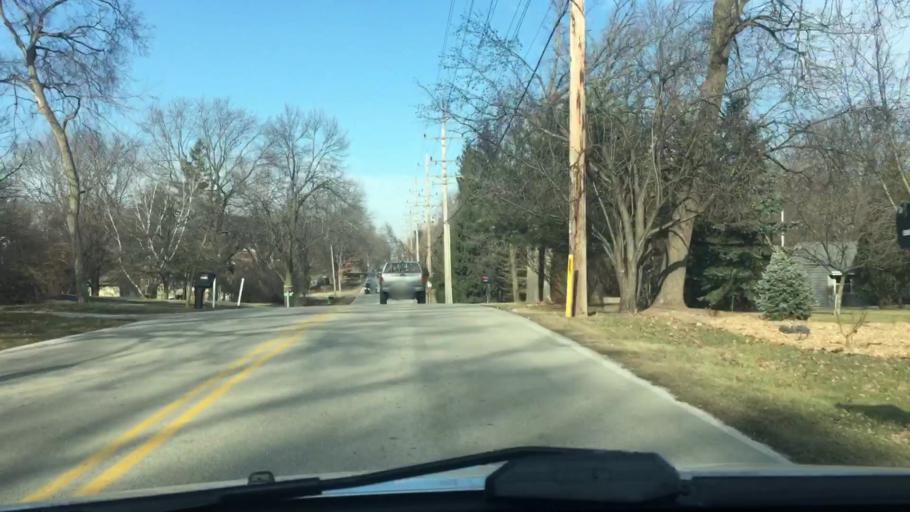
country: US
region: Wisconsin
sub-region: Waukesha County
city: Elm Grove
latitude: 43.0466
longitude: -88.0669
